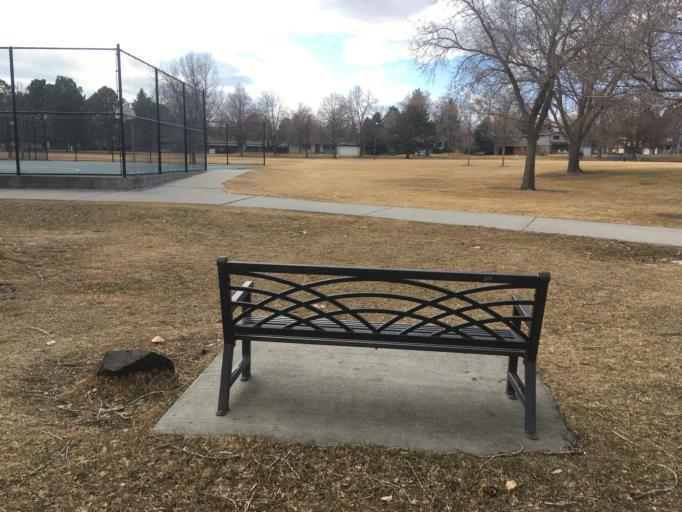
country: US
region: Colorado
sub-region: Broomfield County
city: Broomfield
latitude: 39.9376
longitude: -105.0579
